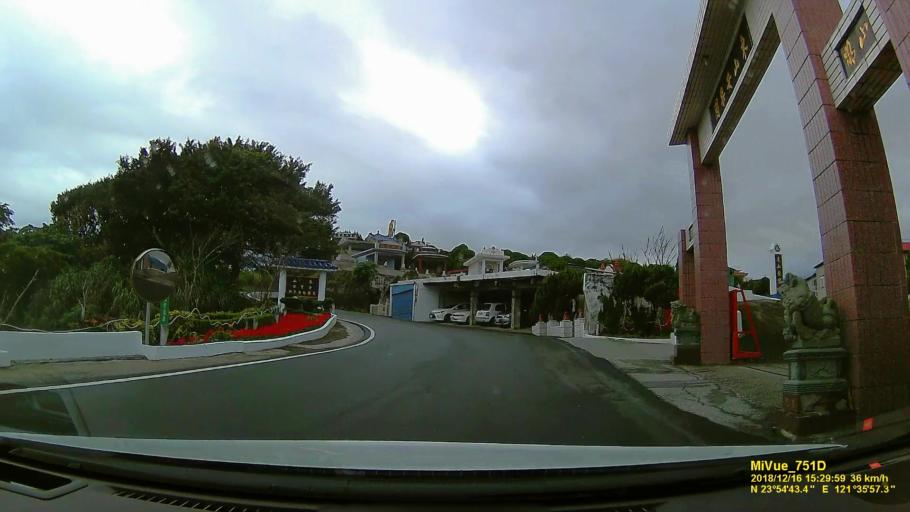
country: TW
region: Taiwan
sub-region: Hualien
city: Hualian
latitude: 23.9121
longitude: 121.5992
